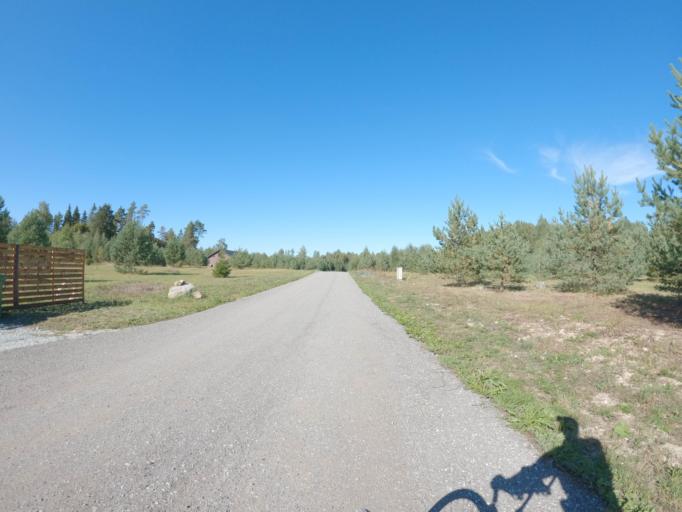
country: EE
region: Raplamaa
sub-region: Rapla vald
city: Rapla
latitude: 58.9884
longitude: 24.8115
